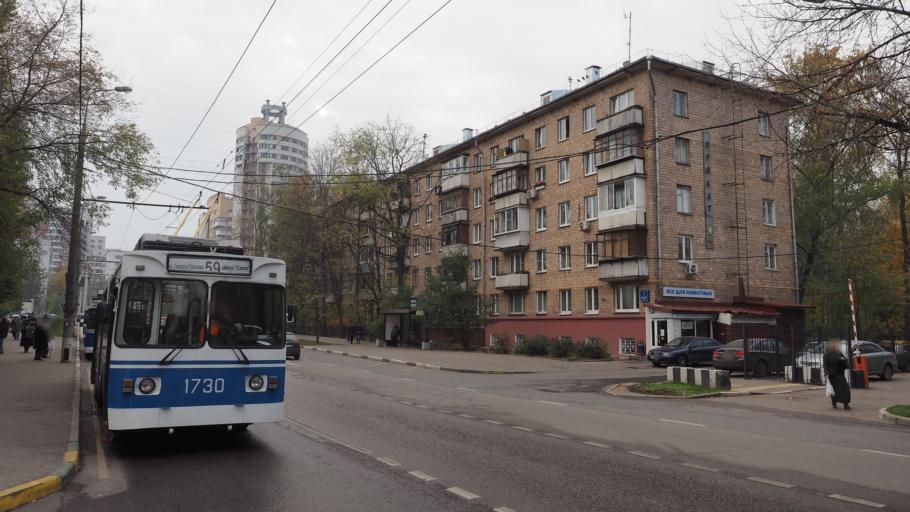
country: RU
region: Moskovskaya
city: Khoroshevo-Mnevniki
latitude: 55.7790
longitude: 37.4608
